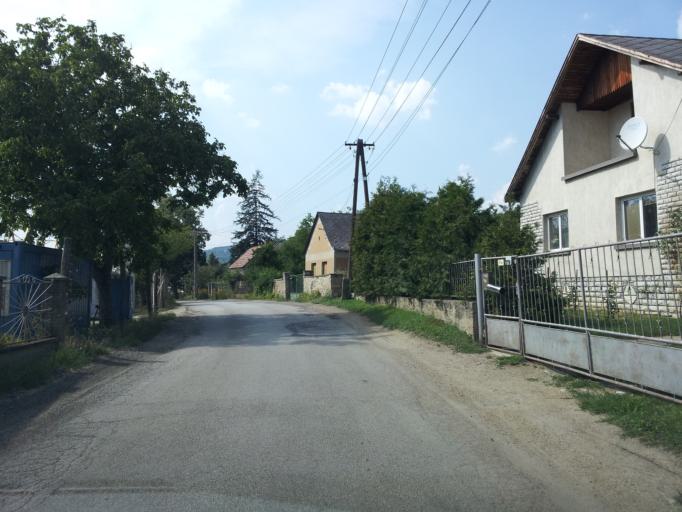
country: HU
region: Veszprem
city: Balatonfured
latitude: 46.9677
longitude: 17.8285
